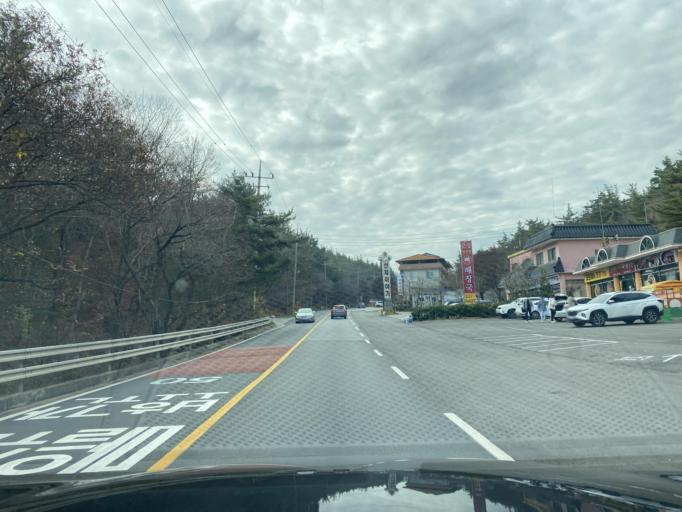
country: KR
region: Chungcheongnam-do
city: Hongsung
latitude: 36.6719
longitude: 126.6420
